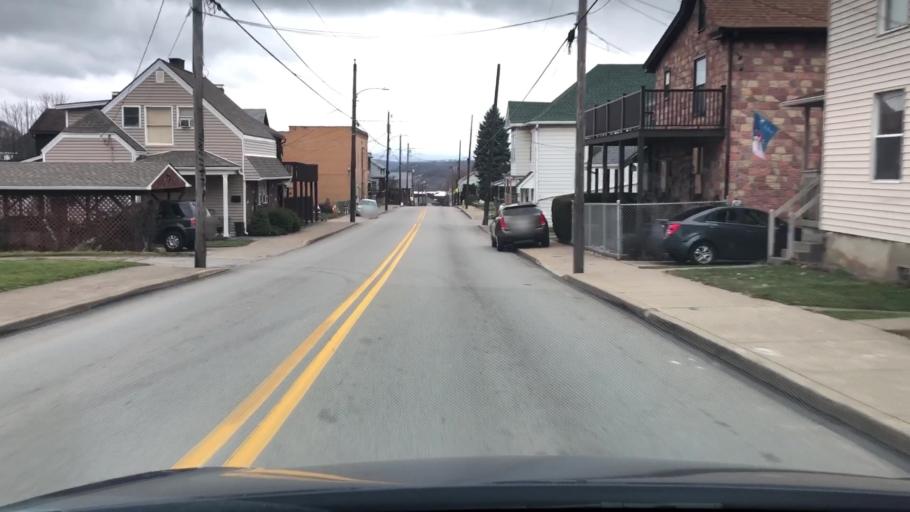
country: US
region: Pennsylvania
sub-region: Fayette County
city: Connellsville
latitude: 40.0214
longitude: -79.5832
